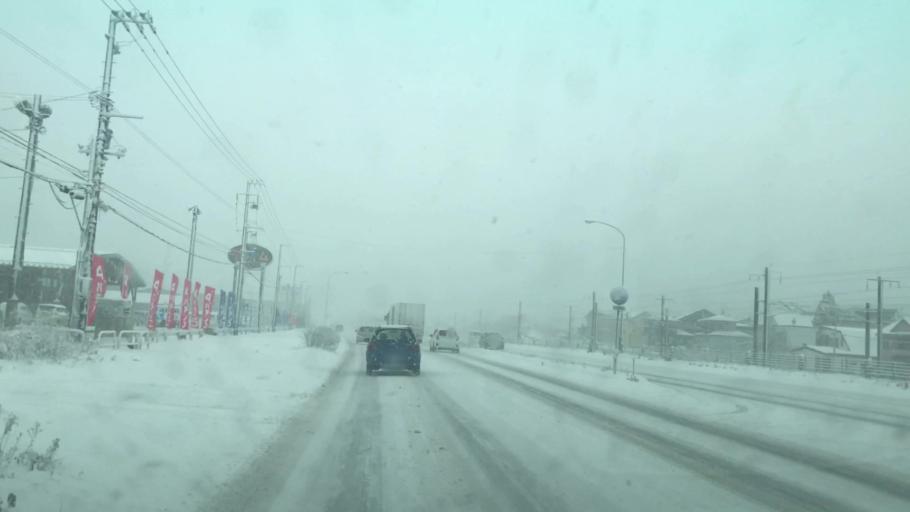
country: JP
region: Hokkaido
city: Muroran
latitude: 42.3879
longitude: 141.0807
